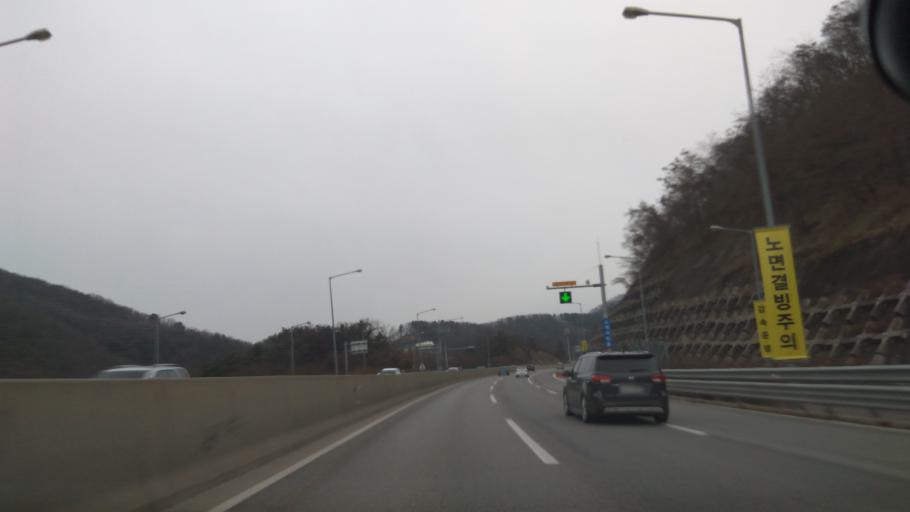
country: KR
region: Gyeonggi-do
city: Hwado
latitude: 37.6345
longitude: 127.3715
